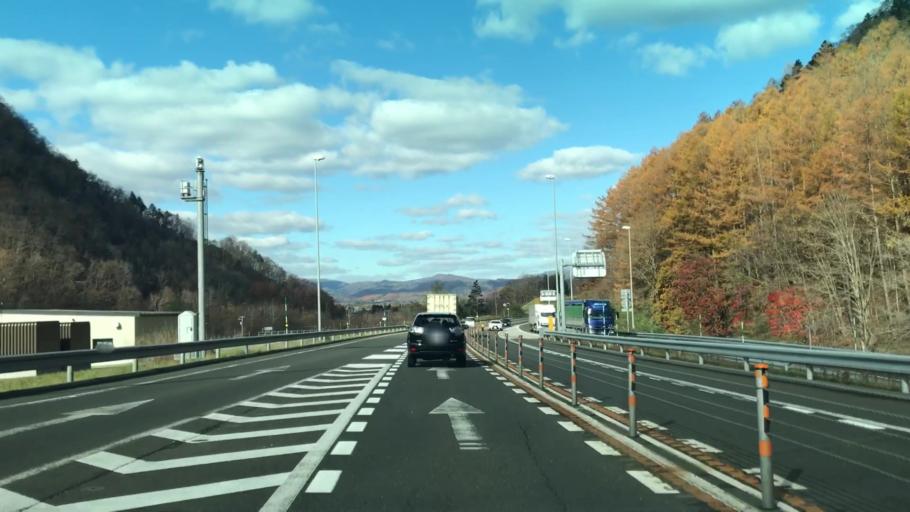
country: JP
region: Hokkaido
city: Iwamizawa
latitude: 42.9246
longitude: 142.0362
